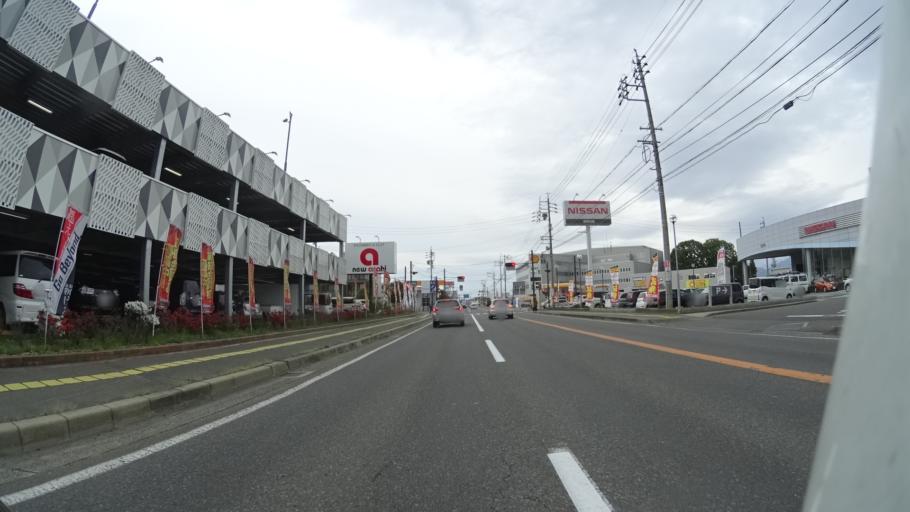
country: JP
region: Nagano
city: Nagano-shi
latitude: 36.6146
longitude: 138.1771
